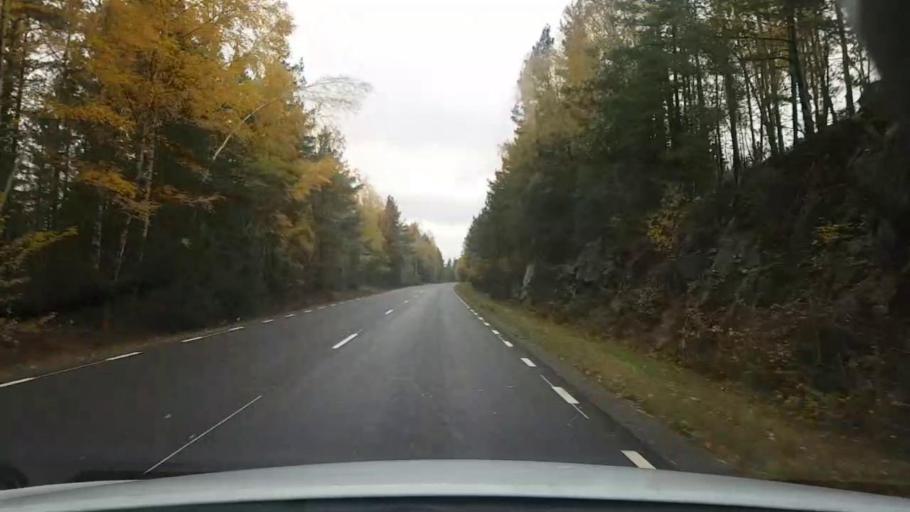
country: SE
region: OErebro
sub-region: Laxa Kommun
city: Laxa
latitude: 58.8399
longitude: 14.5474
